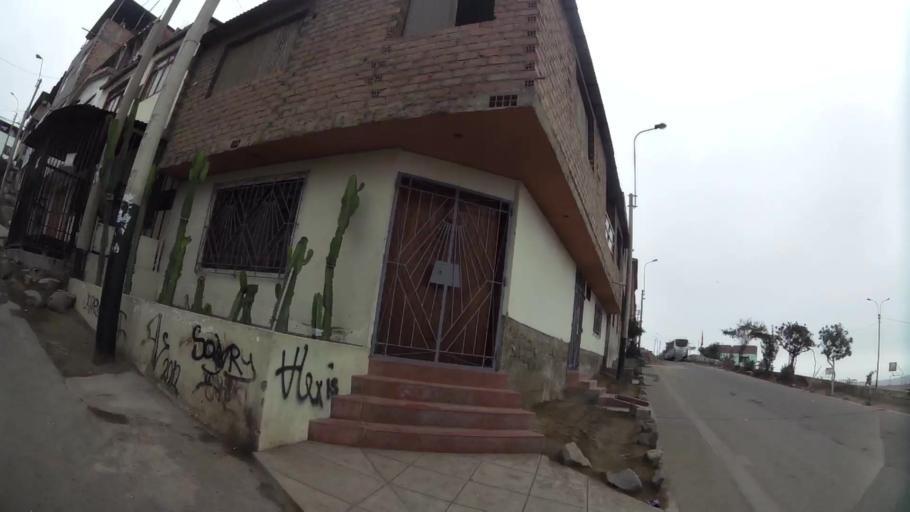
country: PE
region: Lima
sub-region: Lima
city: Surco
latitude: -12.1687
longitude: -76.9589
